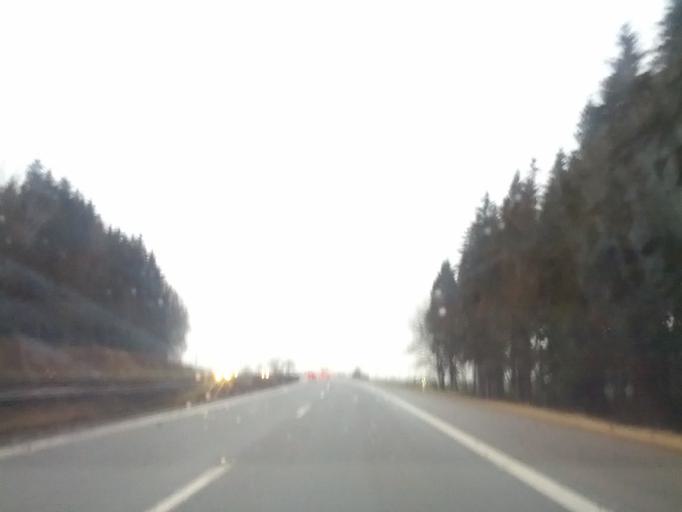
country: DE
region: Bavaria
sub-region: Swabia
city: Bohen
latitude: 47.8605
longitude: 10.2767
